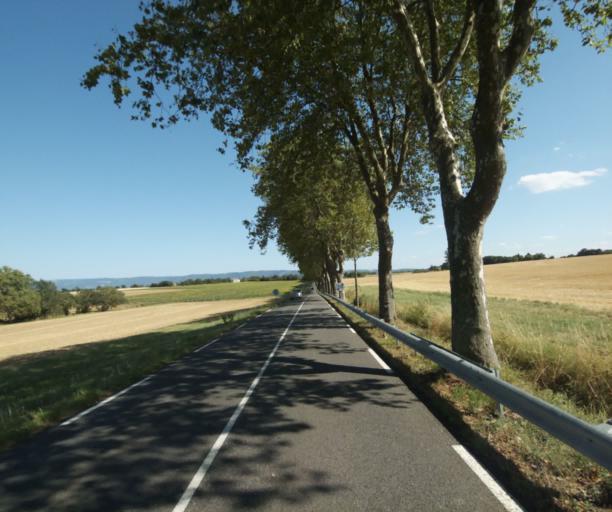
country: FR
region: Midi-Pyrenees
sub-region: Departement de la Haute-Garonne
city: Saint-Felix-Lauragais
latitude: 43.4876
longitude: 1.9076
